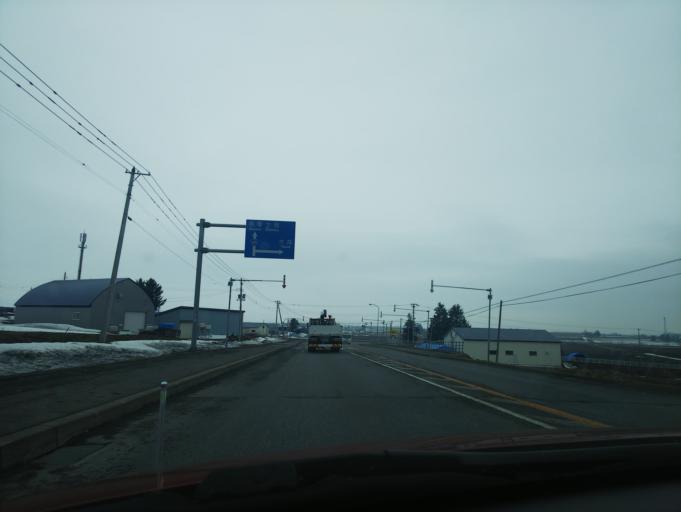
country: JP
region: Hokkaido
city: Nayoro
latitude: 44.0630
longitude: 142.4013
